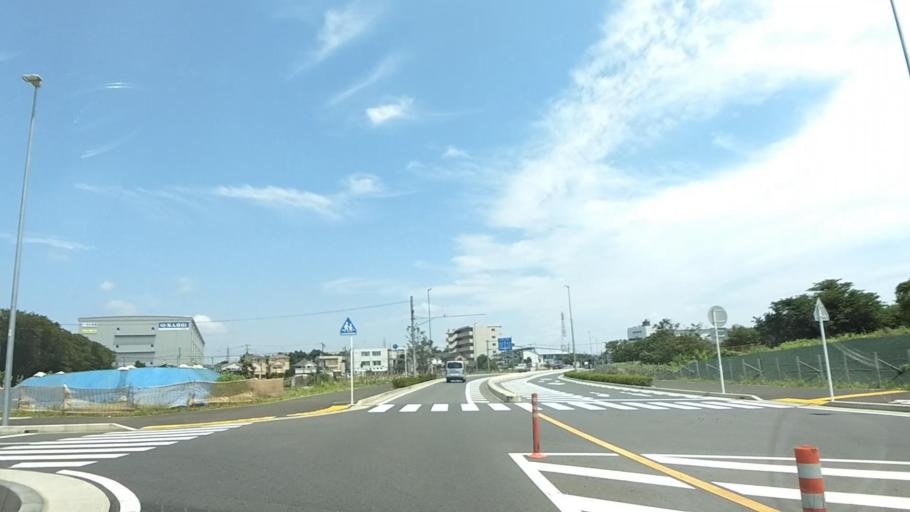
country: JP
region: Kanagawa
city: Minami-rinkan
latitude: 35.4958
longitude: 139.4803
